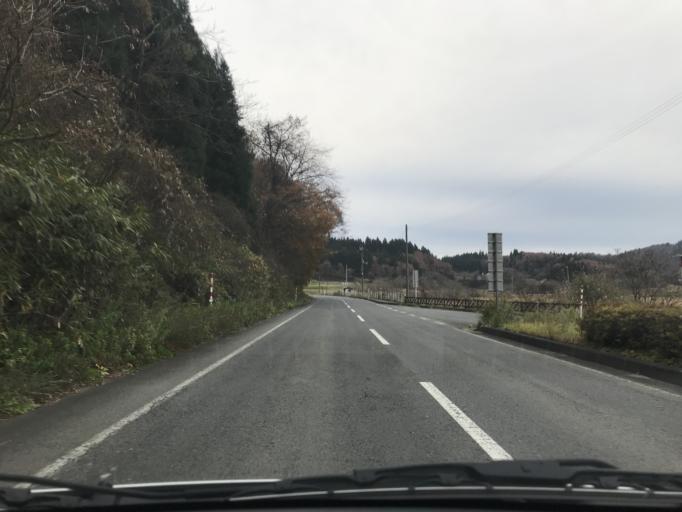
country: JP
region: Iwate
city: Kitakami
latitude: 39.2660
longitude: 141.2682
